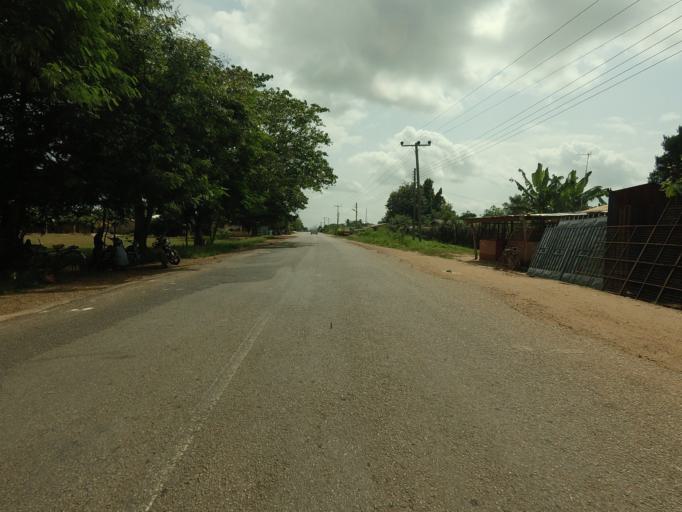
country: TG
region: Maritime
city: Lome
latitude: 6.2209
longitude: 1.0422
